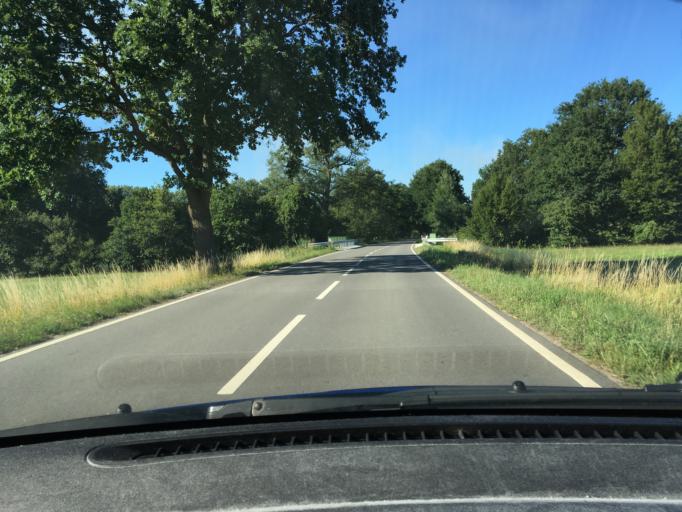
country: DE
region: Lower Saxony
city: Bleckede
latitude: 53.3267
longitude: 10.6759
